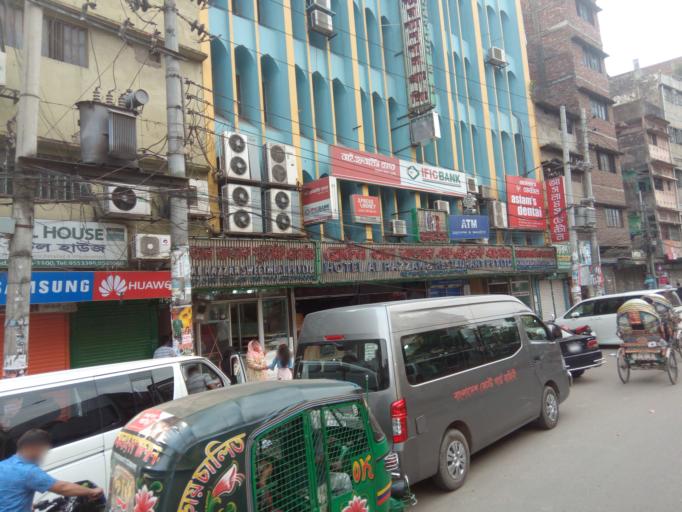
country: BD
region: Dhaka
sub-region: Dhaka
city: Dhaka
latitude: 23.7181
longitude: 90.4086
